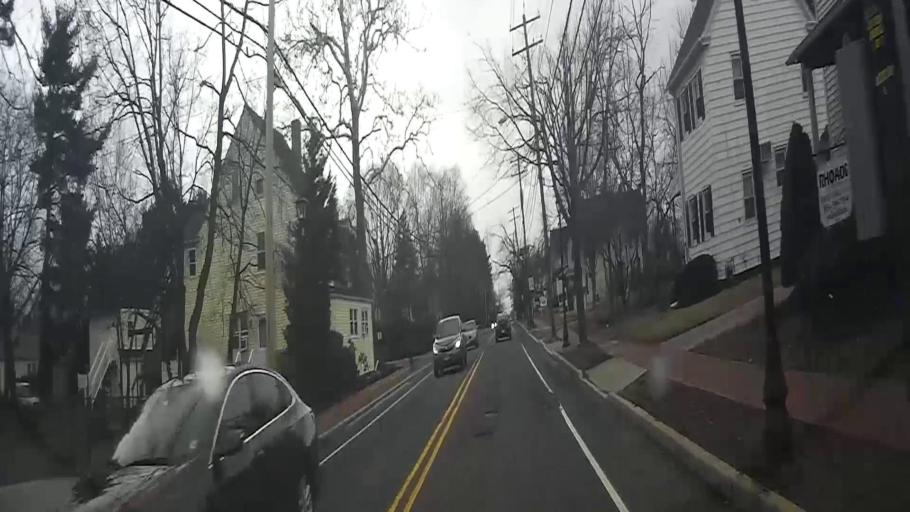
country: US
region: New Jersey
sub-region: Burlington County
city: Marlton
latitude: 39.8888
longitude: -74.9221
